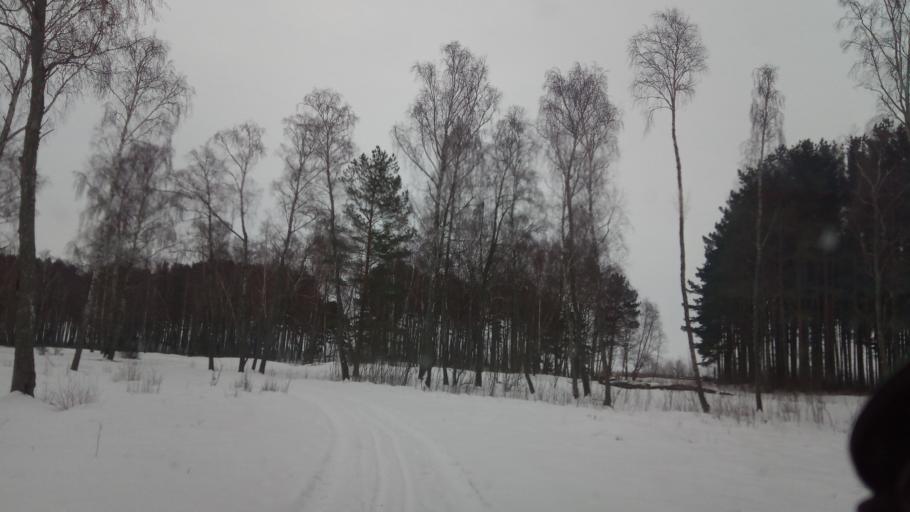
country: LT
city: Neringa
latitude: 55.4181
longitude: 21.1012
